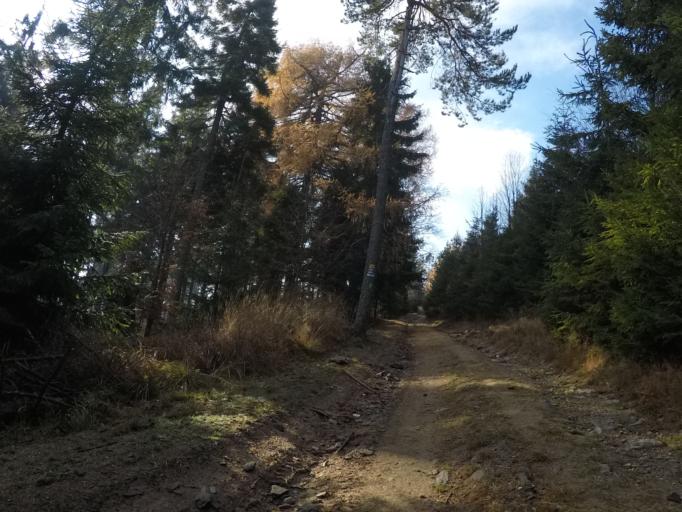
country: SK
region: Kosicky
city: Gelnica
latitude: 48.7592
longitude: 21.0468
